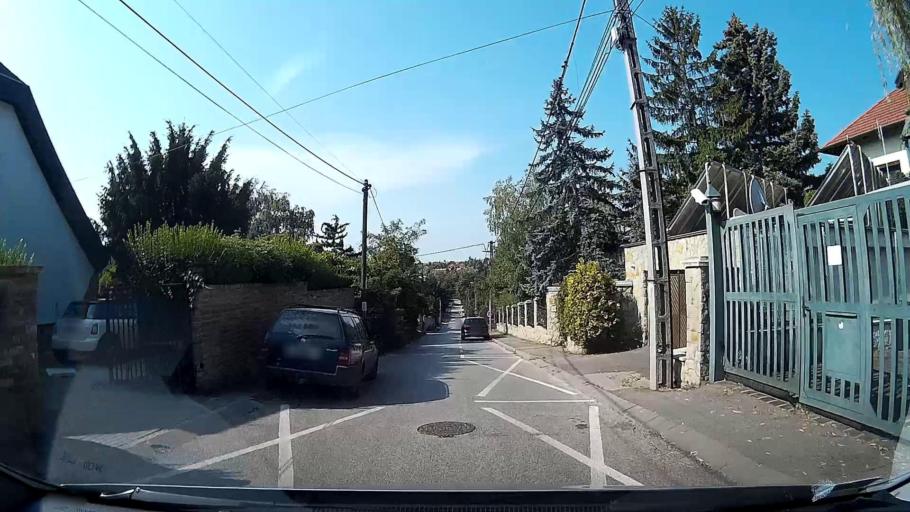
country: HU
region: Pest
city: Szentendre
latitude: 47.6810
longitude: 19.0739
